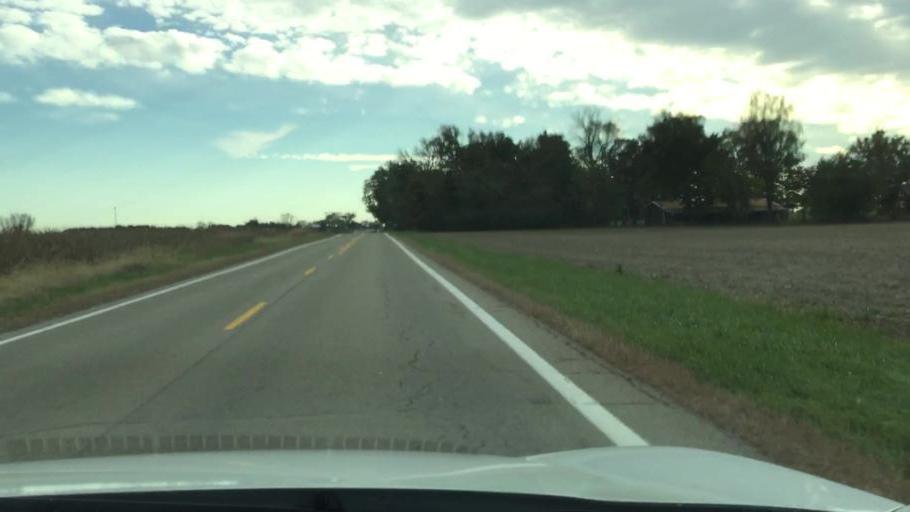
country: US
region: Ohio
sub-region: Champaign County
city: Mechanicsburg
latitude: 40.1066
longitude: -83.5401
